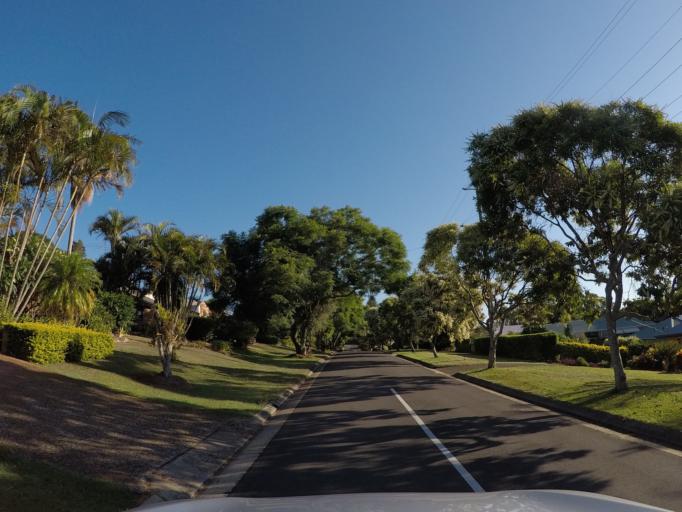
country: AU
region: Queensland
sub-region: Sunshine Coast
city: Nambour
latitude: -26.6184
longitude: 152.8647
